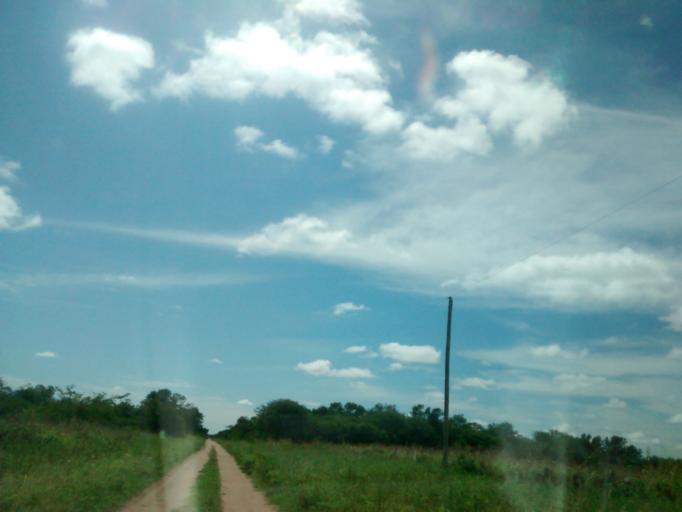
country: AR
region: Chaco
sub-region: Departamento de Quitilipi
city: Quitilipi
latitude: -26.7854
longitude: -60.2178
